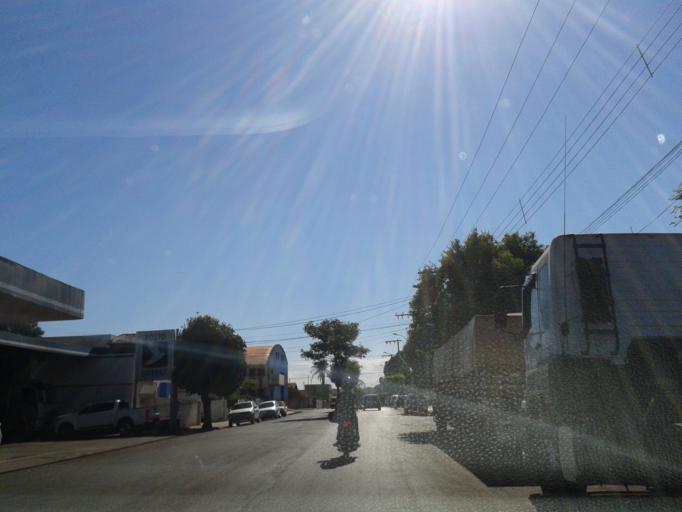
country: BR
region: Minas Gerais
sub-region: Capinopolis
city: Capinopolis
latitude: -18.6845
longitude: -49.5674
